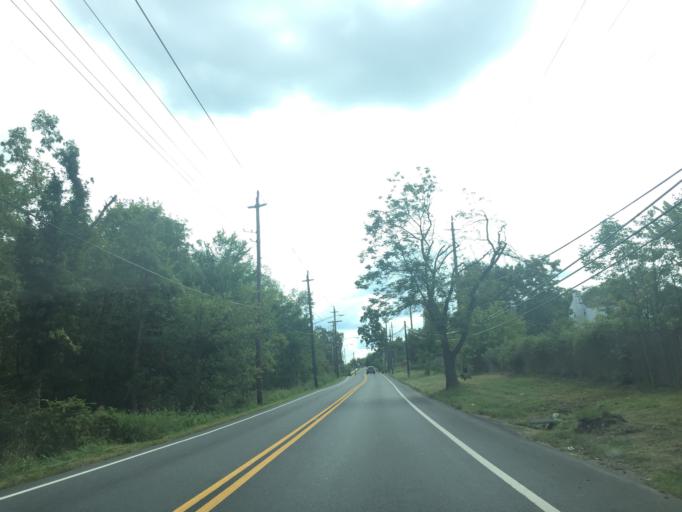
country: US
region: Maryland
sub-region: Montgomery County
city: Redland
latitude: 39.1566
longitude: -77.1569
